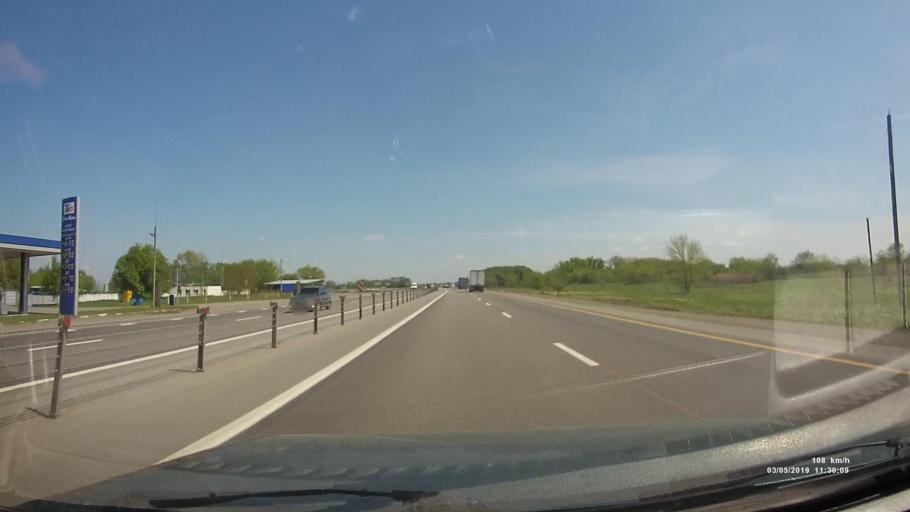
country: RU
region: Rostov
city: Bataysk
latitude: 47.0986
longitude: 39.8101
